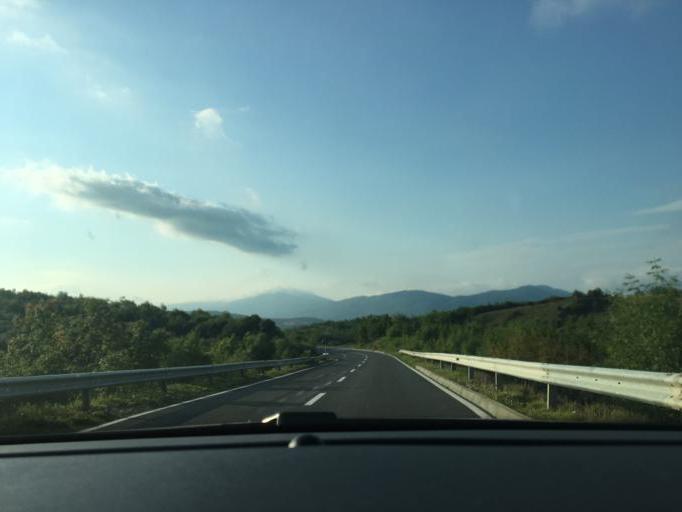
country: MK
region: Valandovo
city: Valandovo
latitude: 41.3321
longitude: 22.5942
